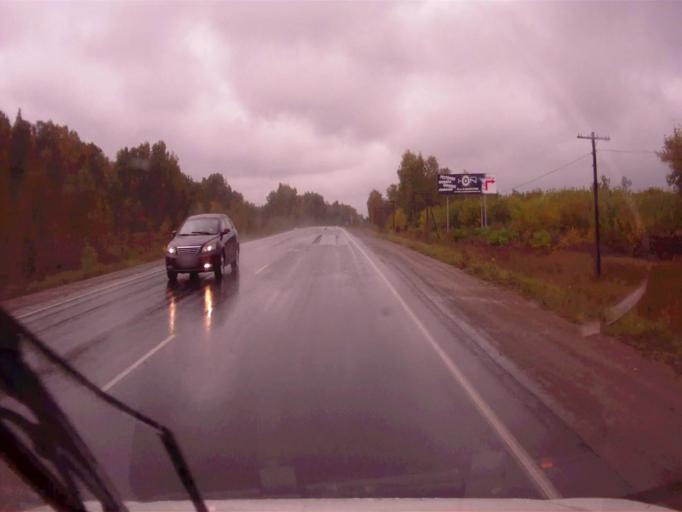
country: RU
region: Chelyabinsk
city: Argayash
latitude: 55.4689
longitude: 60.9057
